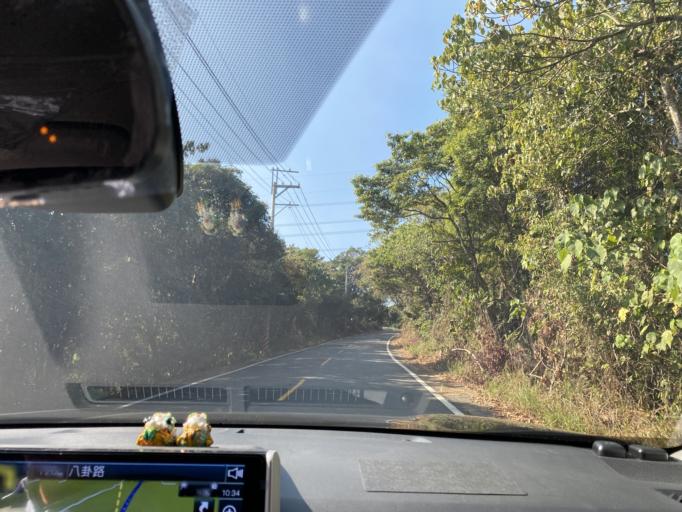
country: TW
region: Taiwan
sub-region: Nantou
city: Nantou
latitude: 23.9371
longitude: 120.6451
